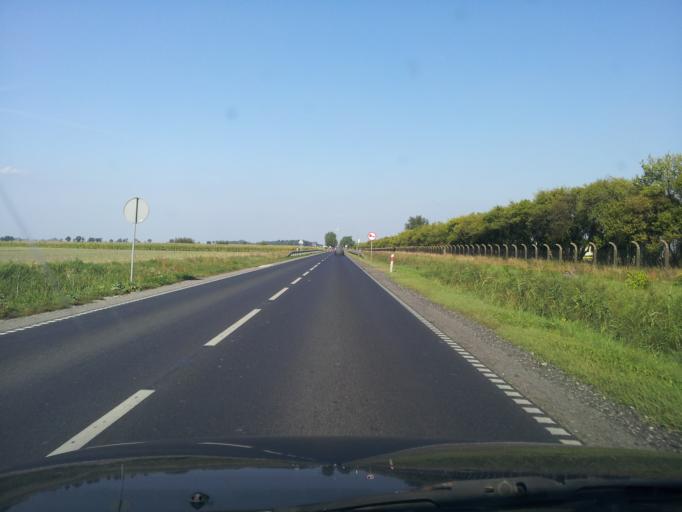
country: PL
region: Kujawsko-Pomorskie
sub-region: Powiat inowroclawski
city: Inowroclaw
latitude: 52.8298
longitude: 18.3110
